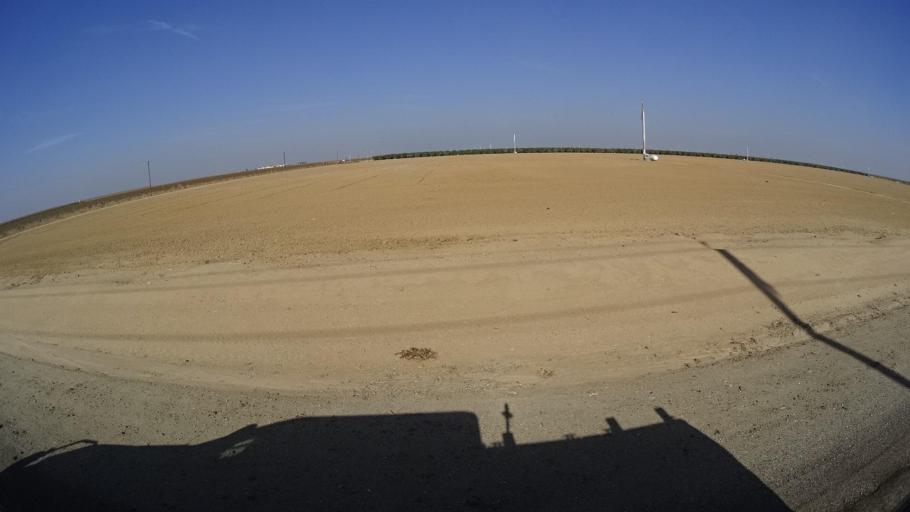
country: US
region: California
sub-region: Kern County
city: Shafter
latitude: 35.5298
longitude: -119.1417
